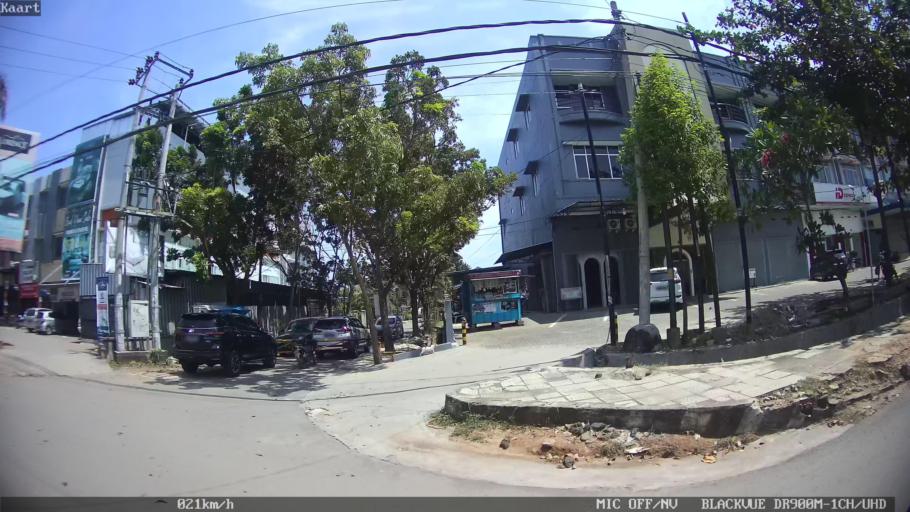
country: ID
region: Lampung
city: Kedaton
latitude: -5.3830
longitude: 105.2797
